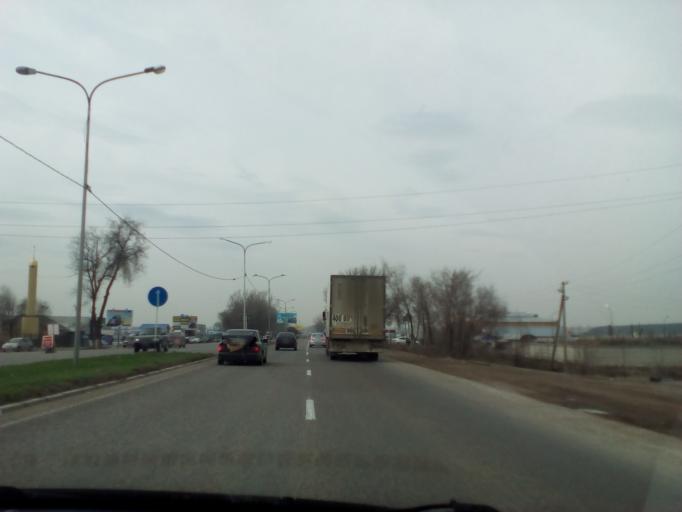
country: KZ
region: Almaty Oblysy
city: Burunday
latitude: 43.2194
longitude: 76.6398
